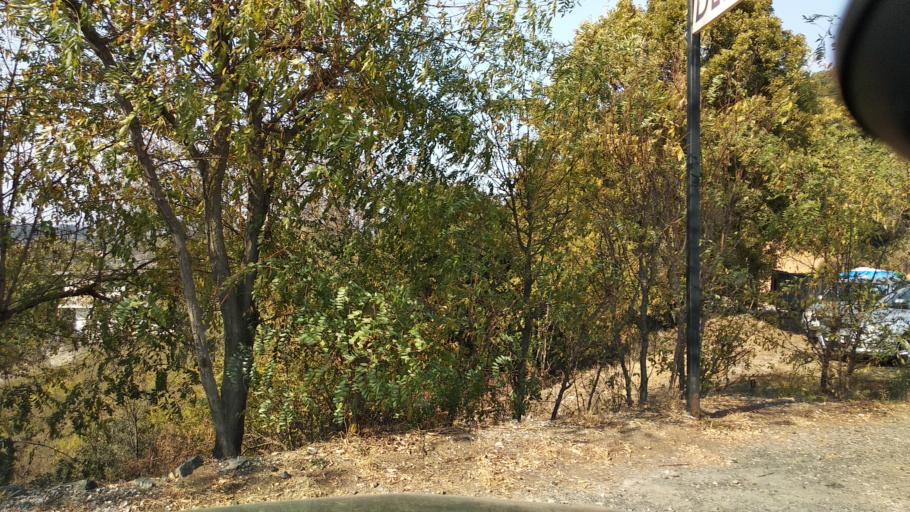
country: GR
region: Thessaly
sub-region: Trikala
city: Kastraki
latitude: 39.7094
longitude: 21.6167
